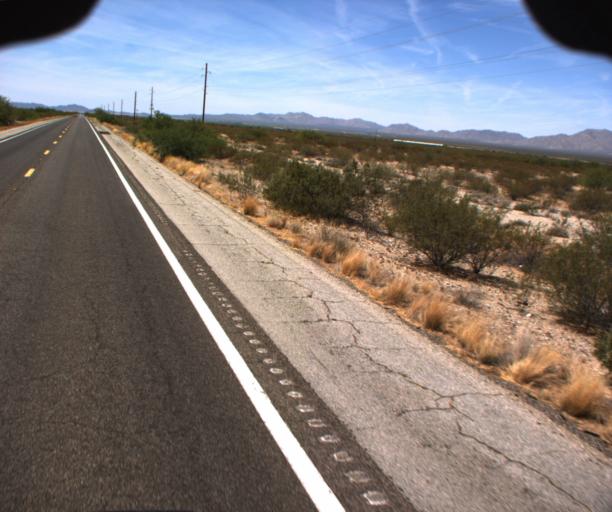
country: US
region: Arizona
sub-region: La Paz County
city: Salome
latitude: 33.8509
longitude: -113.4491
